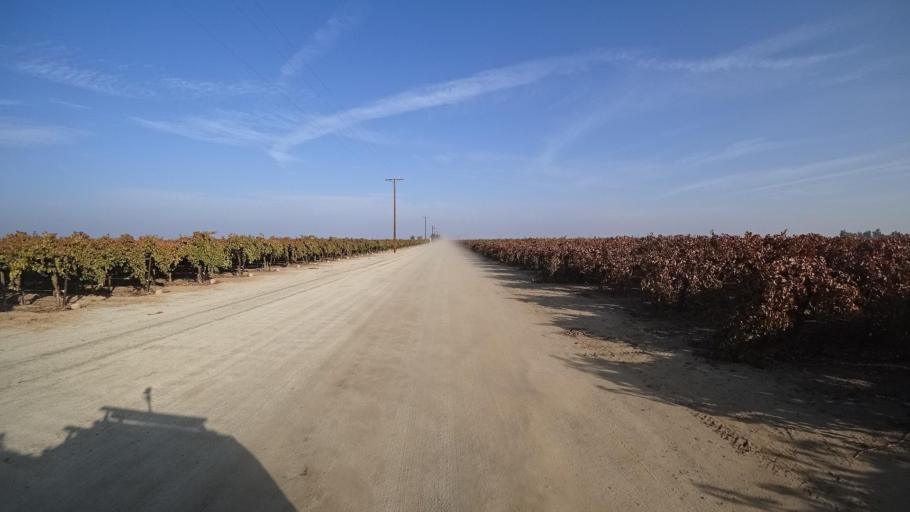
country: US
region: California
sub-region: Kern County
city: Delano
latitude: 35.7409
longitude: -119.1873
